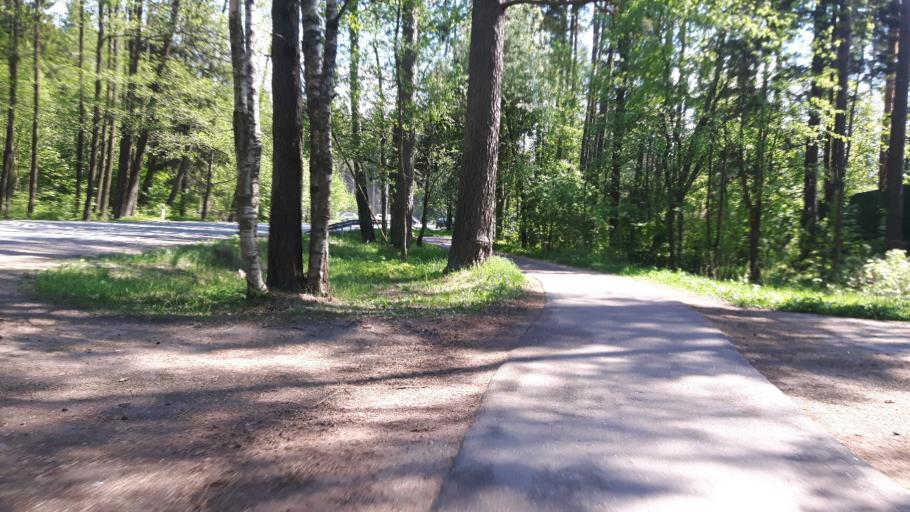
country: RU
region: St.-Petersburg
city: Komarovo
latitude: 60.1715
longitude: 29.8116
